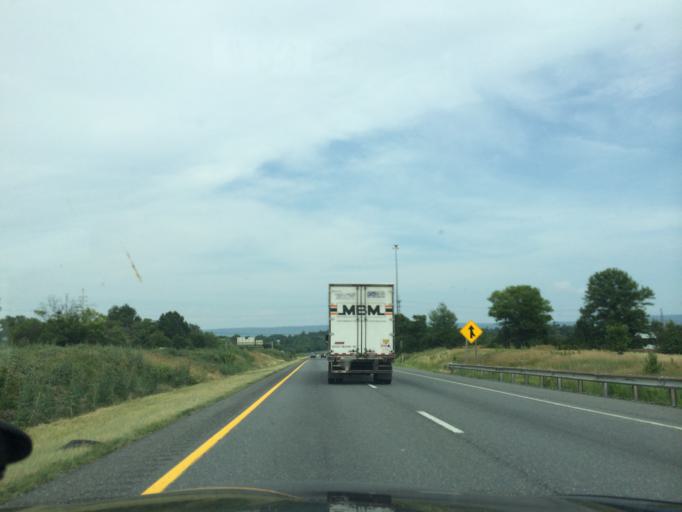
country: US
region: Maryland
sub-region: Washington County
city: Robinwood
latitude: 39.6001
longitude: -77.6804
